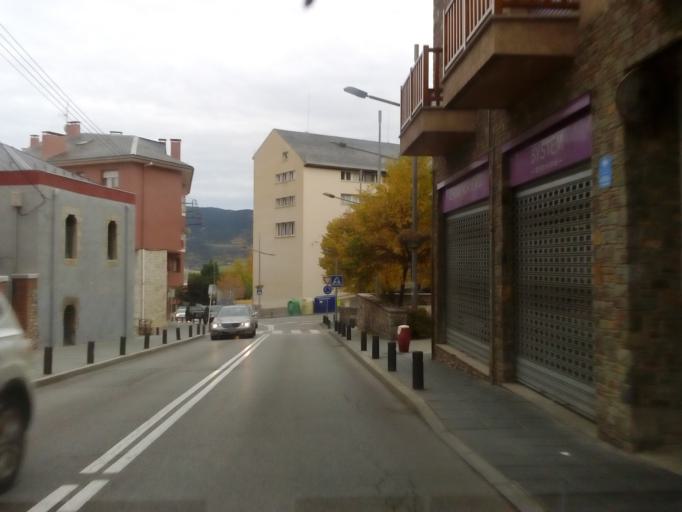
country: ES
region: Catalonia
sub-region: Provincia de Girona
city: Puigcerda
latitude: 42.4339
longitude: 1.9298
